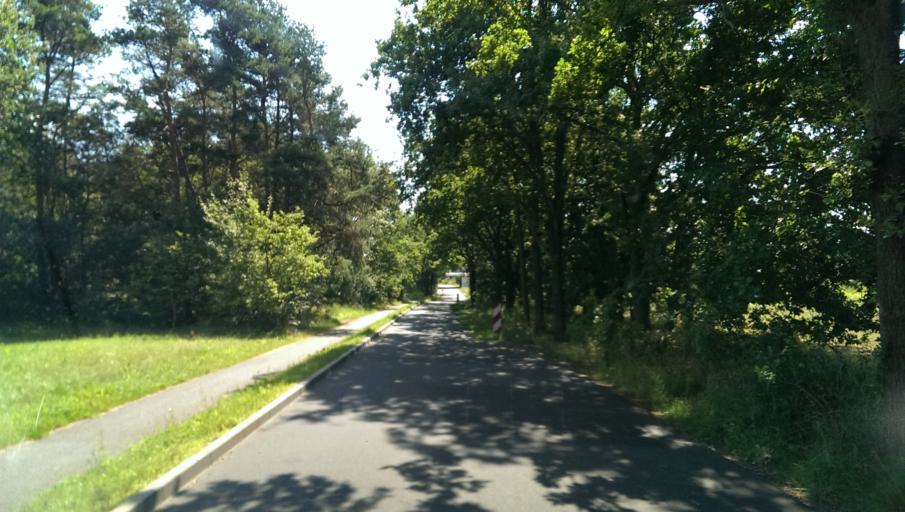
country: DE
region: Brandenburg
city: Michendorf
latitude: 52.3033
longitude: 13.0621
